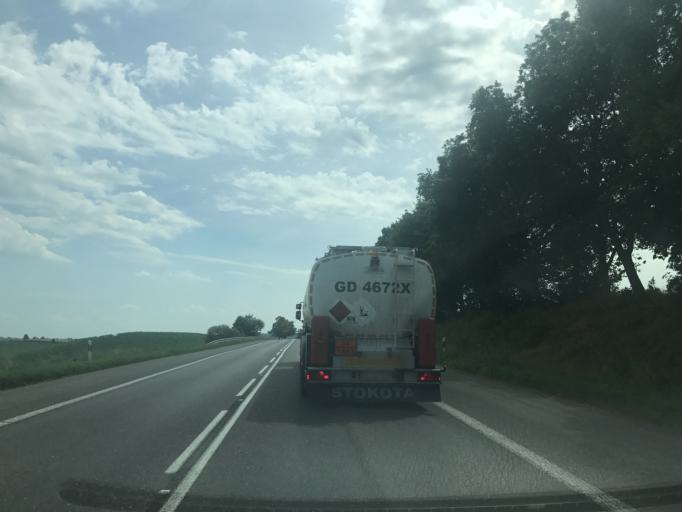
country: PL
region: Warmian-Masurian Voivodeship
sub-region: Powiat ostrodzki
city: Ostroda
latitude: 53.6572
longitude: 20.0502
